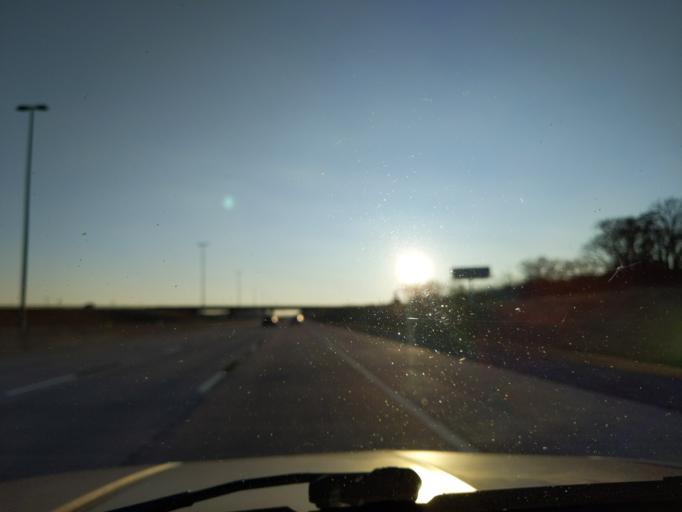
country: US
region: Oklahoma
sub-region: Creek County
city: Kellyville
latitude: 35.9162
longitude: -96.2921
